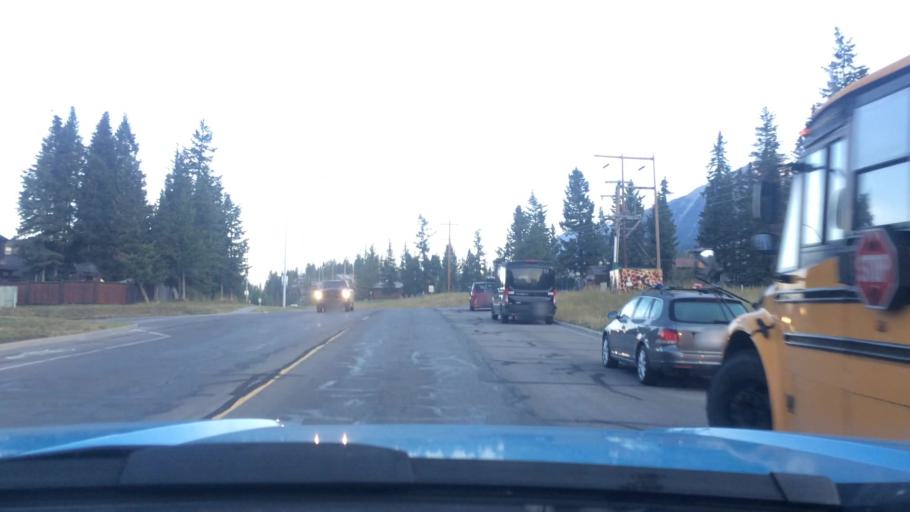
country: CA
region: Alberta
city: Canmore
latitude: 51.0842
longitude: -115.3243
